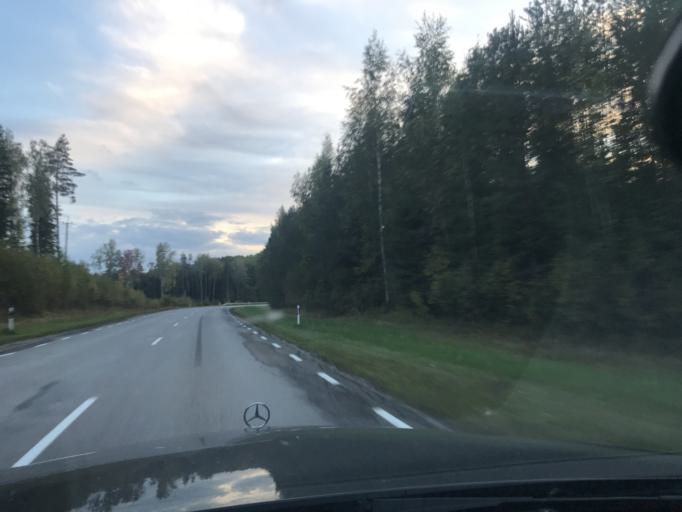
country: EE
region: Valgamaa
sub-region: Torva linn
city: Torva
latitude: 57.9944
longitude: 26.0746
